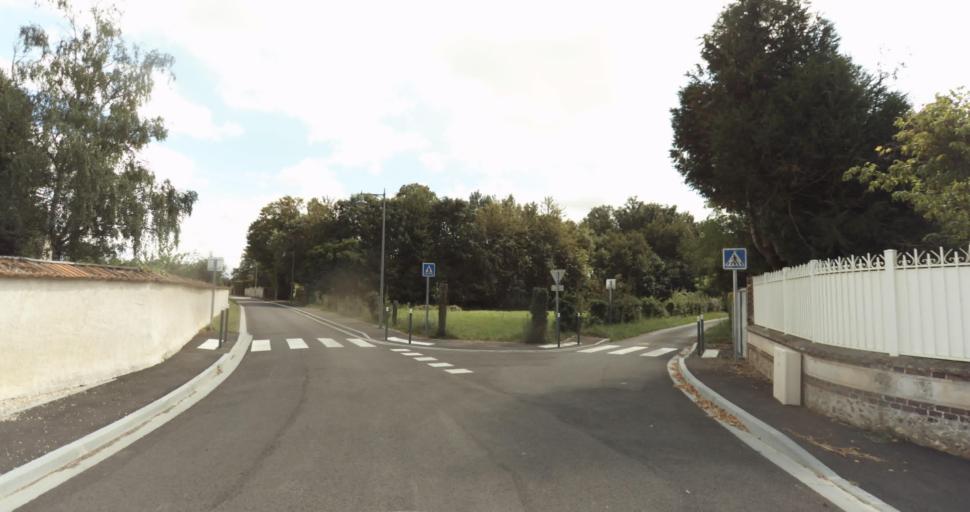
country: FR
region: Haute-Normandie
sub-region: Departement de l'Eure
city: Nonancourt
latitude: 48.8432
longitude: 1.1630
